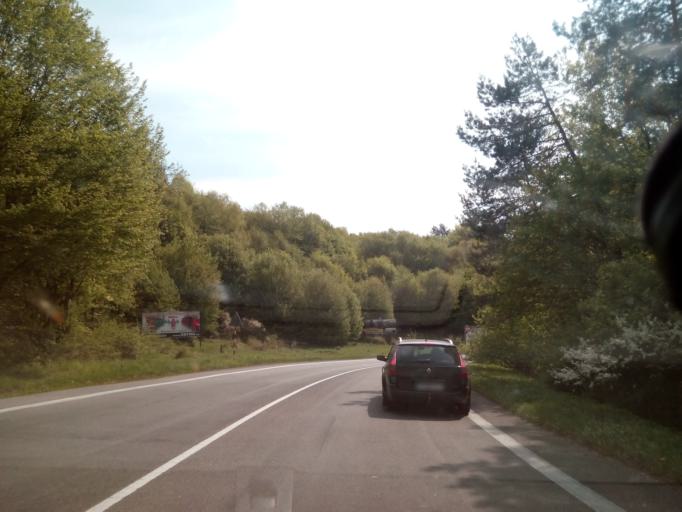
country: SK
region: Presovsky
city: Giraltovce
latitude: 49.0513
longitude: 21.4270
